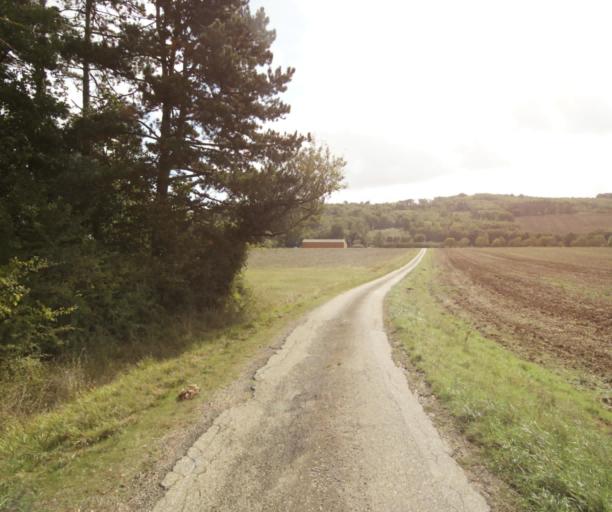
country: FR
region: Midi-Pyrenees
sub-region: Departement du Tarn-et-Garonne
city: Finhan
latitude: 43.8728
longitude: 1.1195
